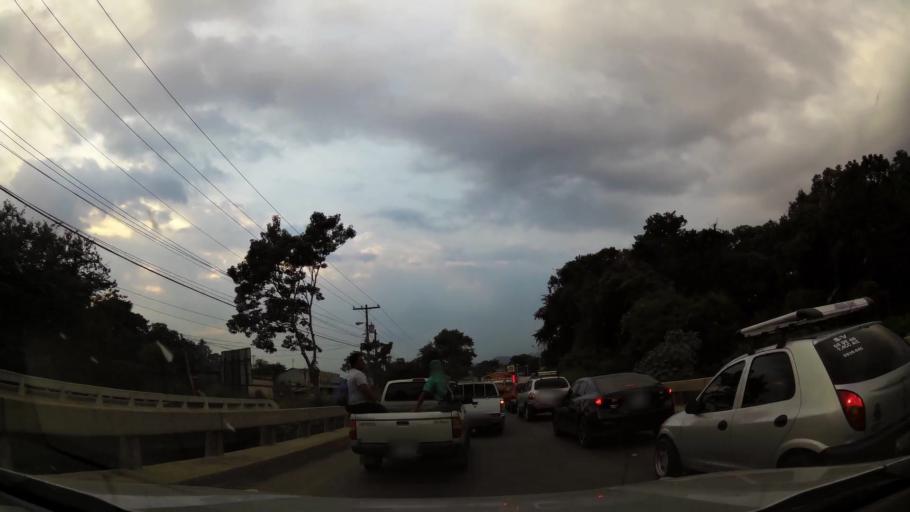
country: GT
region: Escuintla
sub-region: Municipio de Escuintla
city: Escuintla
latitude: 14.2847
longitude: -90.7912
